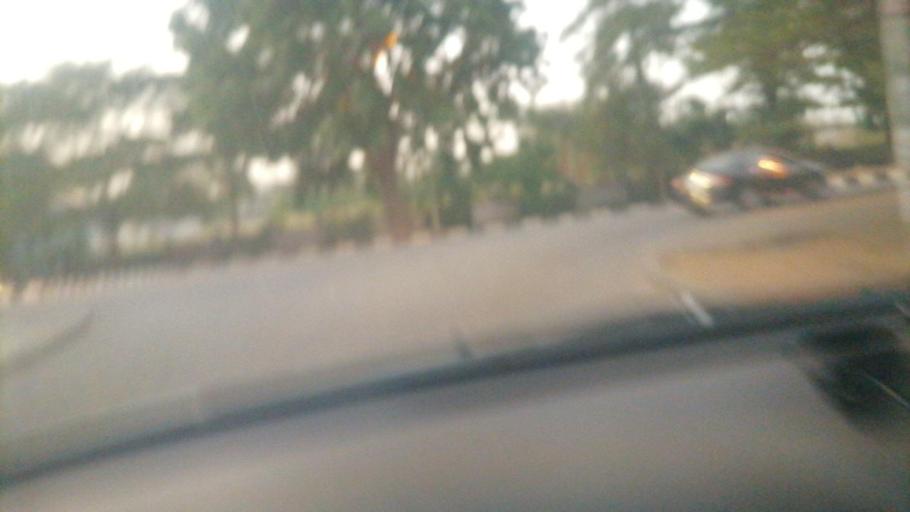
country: NG
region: Abuja Federal Capital Territory
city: Abuja
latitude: 9.0395
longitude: 7.4915
